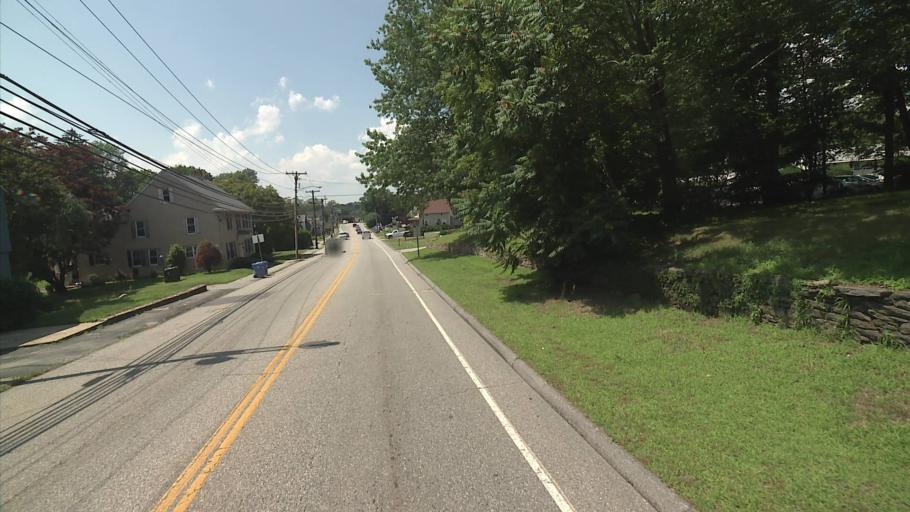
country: US
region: Connecticut
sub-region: New London County
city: Norwich
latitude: 41.5512
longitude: -72.1020
